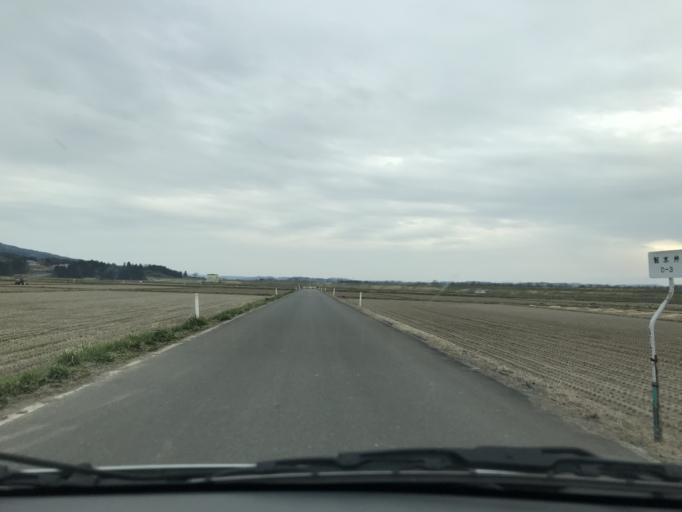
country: JP
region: Iwate
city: Mizusawa
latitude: 39.0560
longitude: 141.1644
